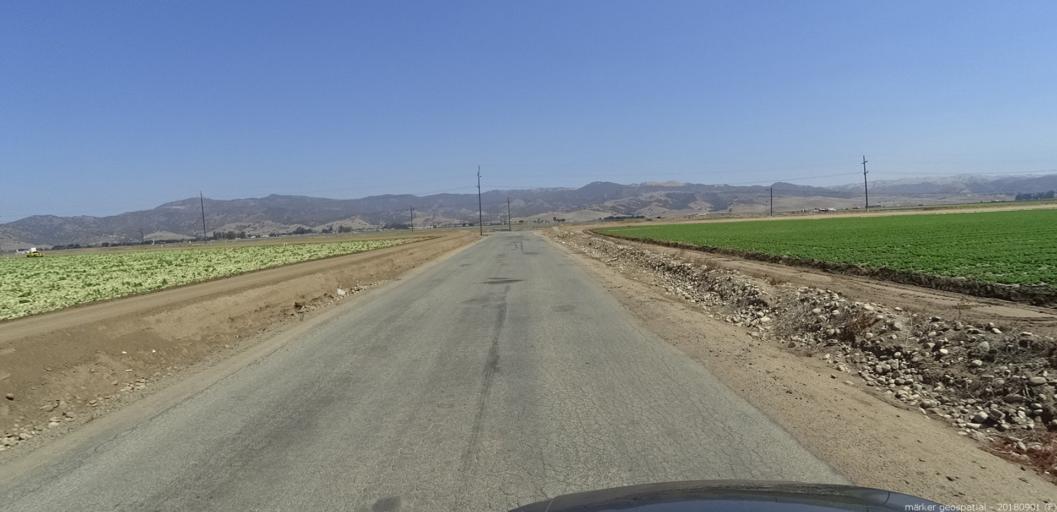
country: US
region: California
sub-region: Monterey County
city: Chualar
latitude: 36.6021
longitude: -121.5136
